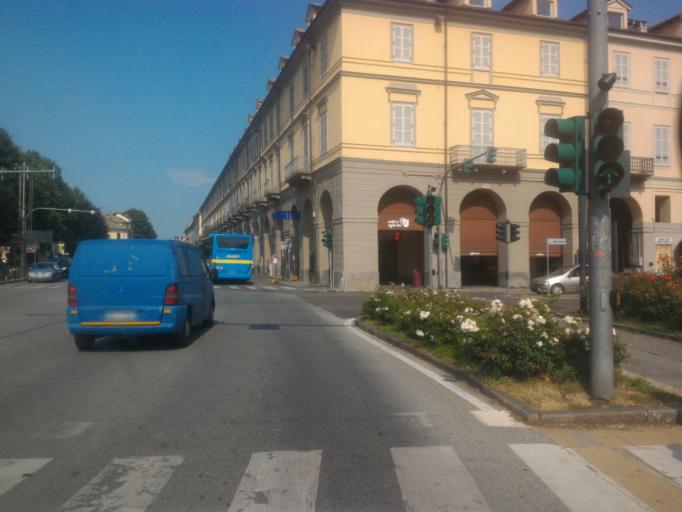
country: IT
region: Piedmont
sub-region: Provincia di Torino
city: Pinerolo
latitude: 44.8845
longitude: 7.3306
